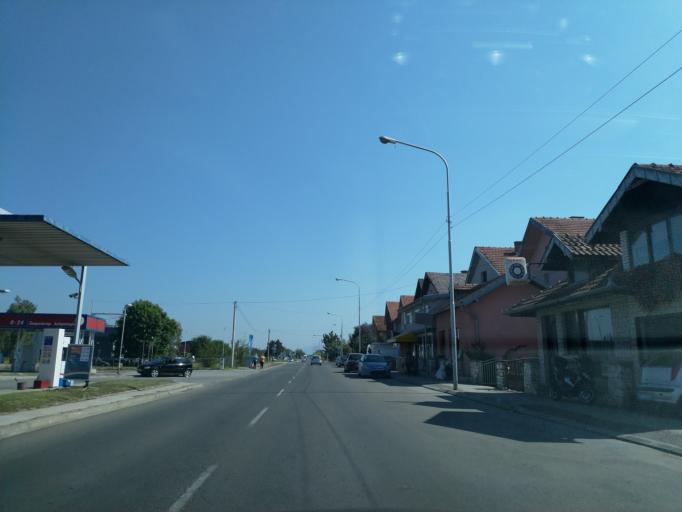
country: RS
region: Central Serbia
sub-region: Rasinski Okrug
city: Trstenik
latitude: 43.6159
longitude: 21.0114
